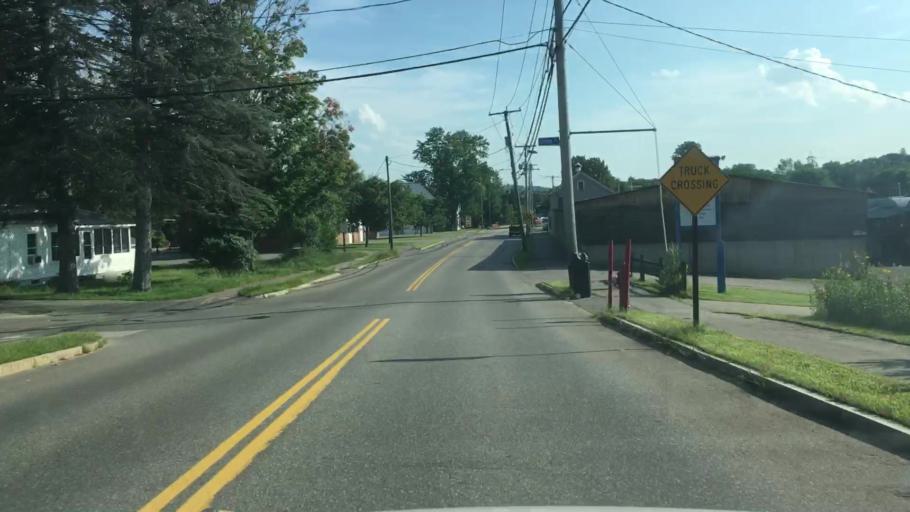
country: US
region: New Hampshire
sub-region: Belknap County
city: Laconia
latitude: 43.5394
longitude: -71.4663
